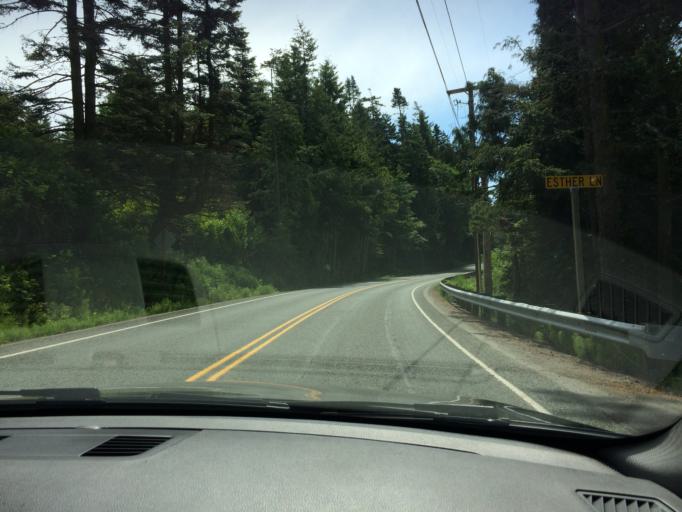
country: US
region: Washington
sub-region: Skagit County
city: Anacortes
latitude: 48.4745
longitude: -122.6562
